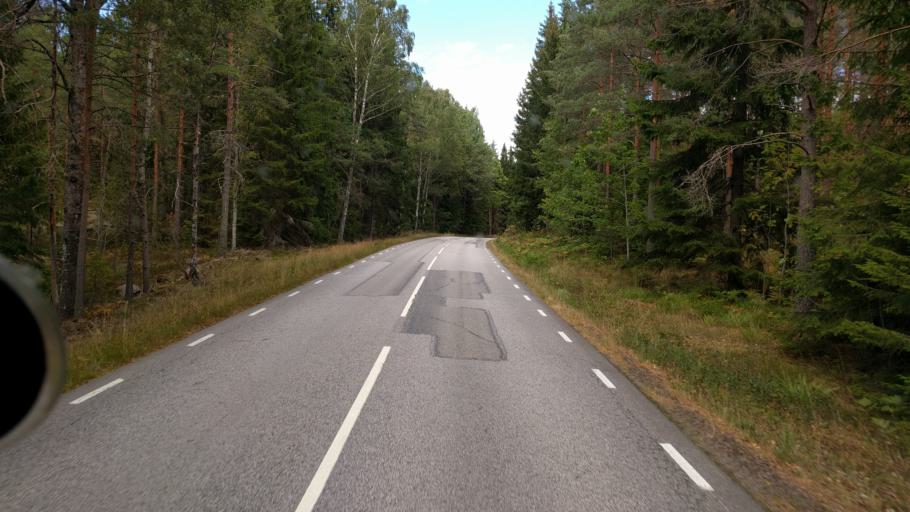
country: SE
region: Kalmar
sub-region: Vasterviks Kommun
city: Ankarsrum
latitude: 57.7486
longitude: 16.1142
